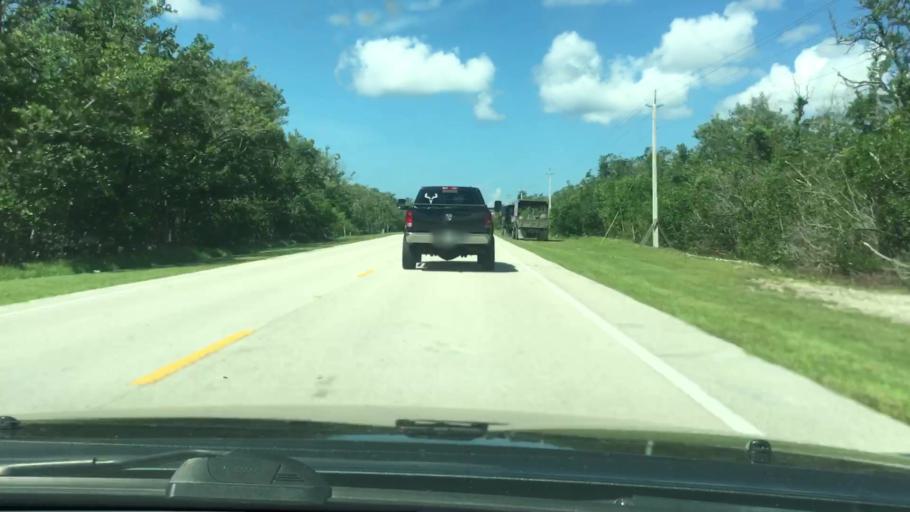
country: US
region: Florida
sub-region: Collier County
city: Marco
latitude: 25.9320
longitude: -81.6653
